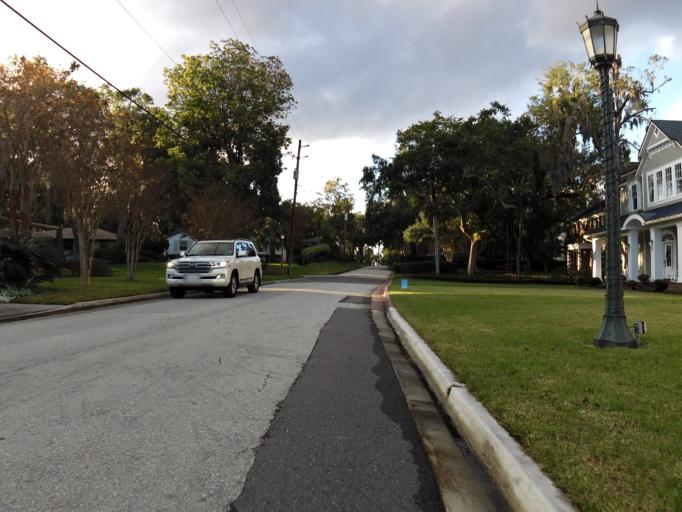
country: US
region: Florida
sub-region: Duval County
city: Jacksonville
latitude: 30.2841
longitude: -81.6571
